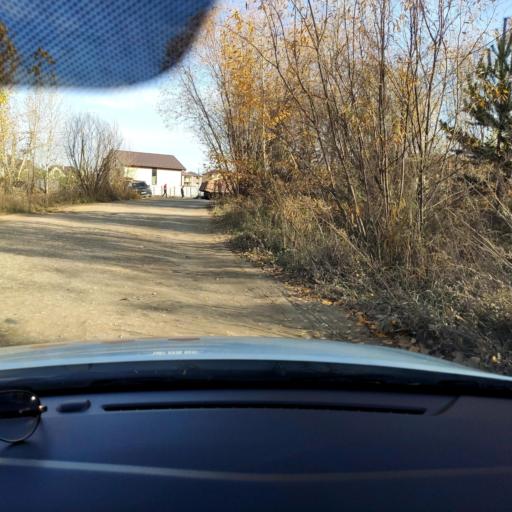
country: RU
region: Tatarstan
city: Vysokaya Gora
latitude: 55.7863
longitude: 49.2604
